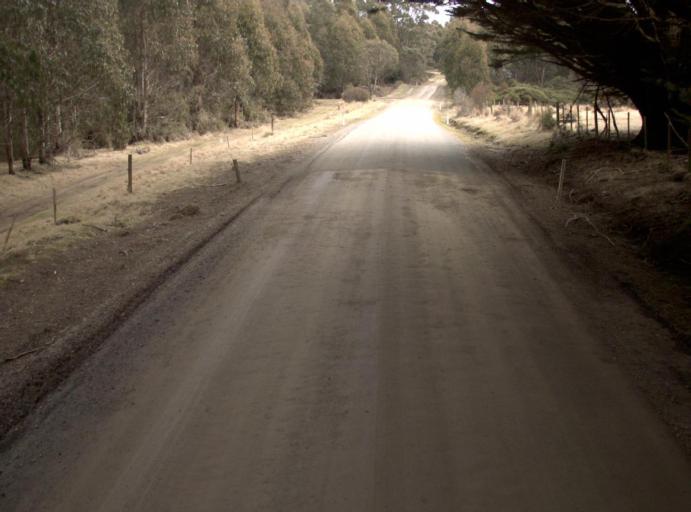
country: AU
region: Tasmania
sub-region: Dorset
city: Scottsdale
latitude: -41.3261
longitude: 147.4772
